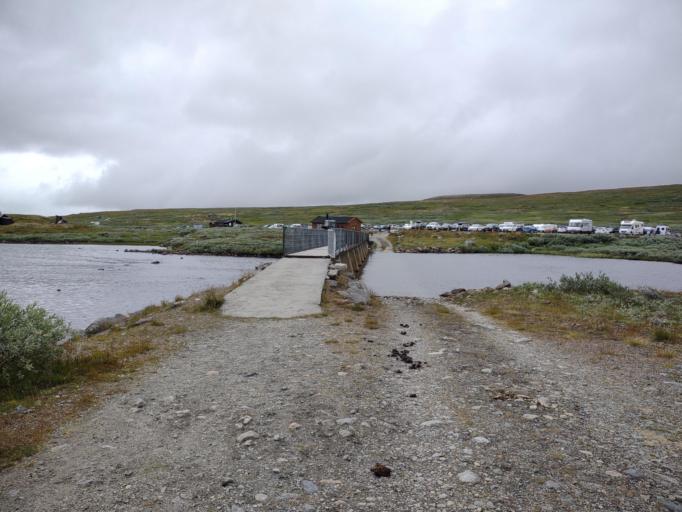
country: NO
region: Hordaland
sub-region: Eidfjord
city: Eidfjord
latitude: 60.2862
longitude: 7.5610
